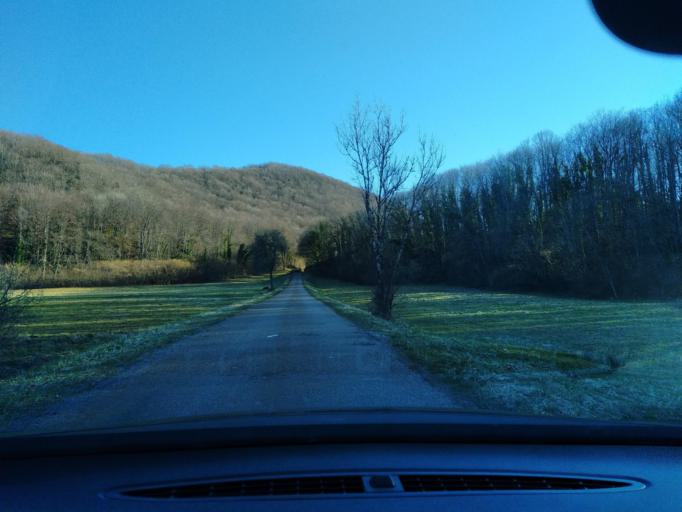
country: FR
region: Franche-Comte
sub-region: Departement du Jura
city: Clairvaux-les-Lacs
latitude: 46.6935
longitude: 5.7275
